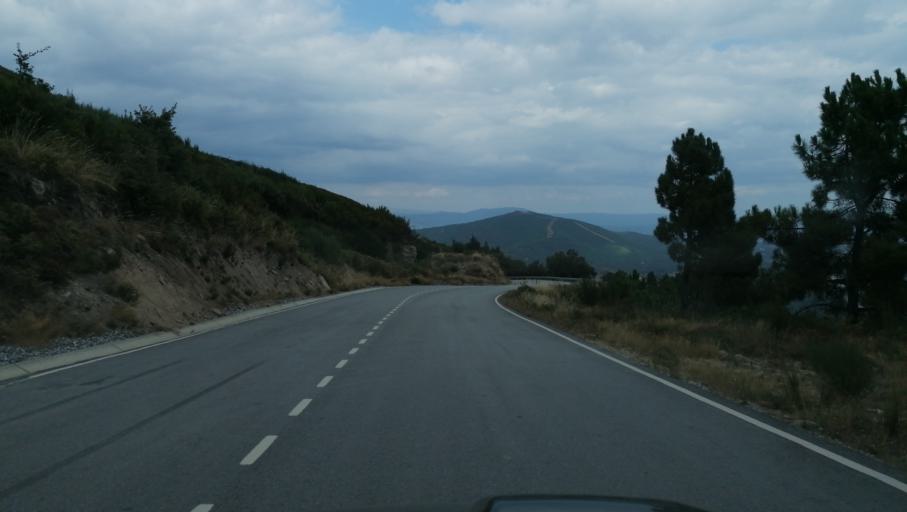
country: PT
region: Vila Real
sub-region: Vila Pouca de Aguiar
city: Vila Pouca de Aguiar
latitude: 41.5550
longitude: -7.6590
